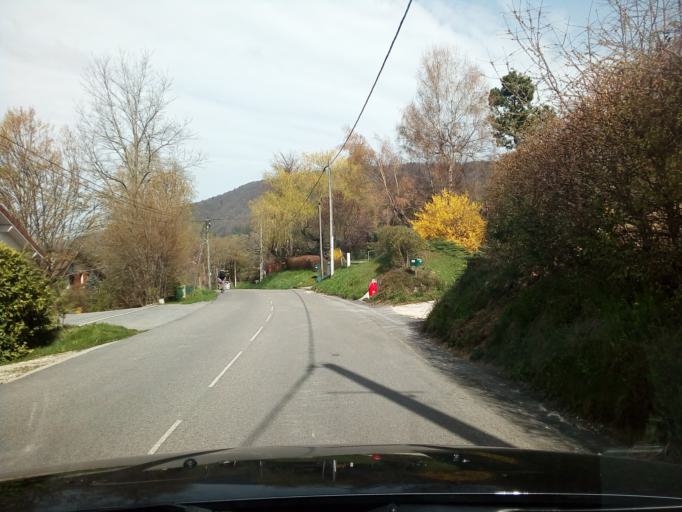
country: FR
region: Rhone-Alpes
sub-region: Departement de l'Isere
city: Revel
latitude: 45.1593
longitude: 5.8475
